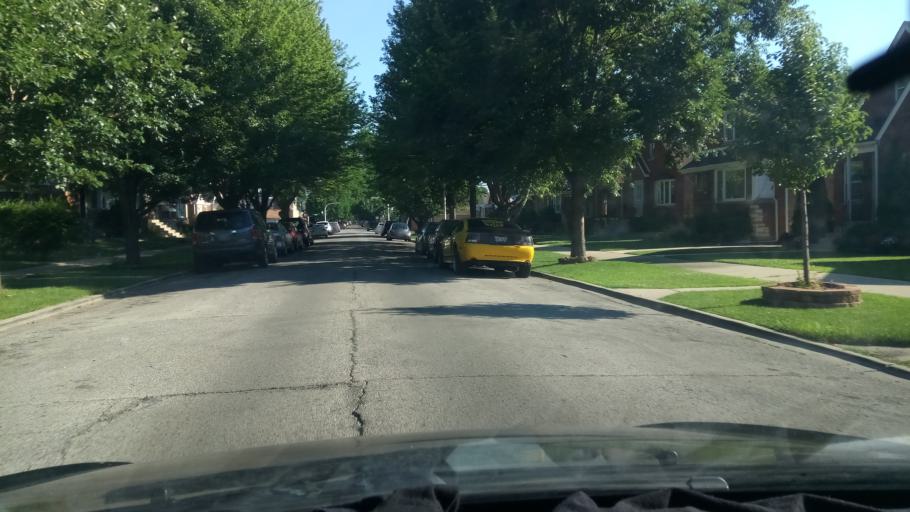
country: US
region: Illinois
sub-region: Cook County
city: Hometown
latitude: 41.7695
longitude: -87.7261
